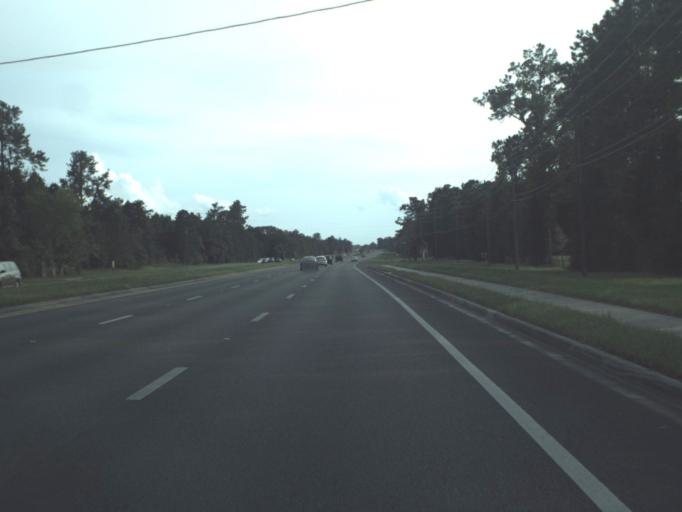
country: US
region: Florida
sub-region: Hernando County
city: South Brooksville
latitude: 28.5227
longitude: -82.4137
